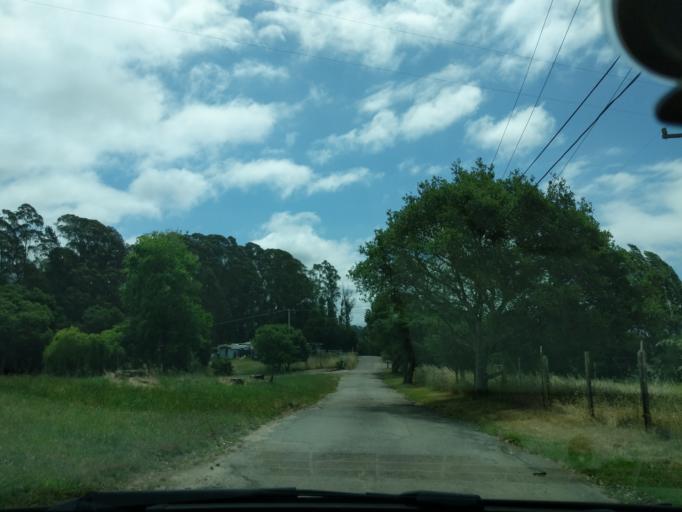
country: US
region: California
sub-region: Santa Cruz County
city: Aptos Hills-Larkin Valley
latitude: 36.9456
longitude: -121.8118
